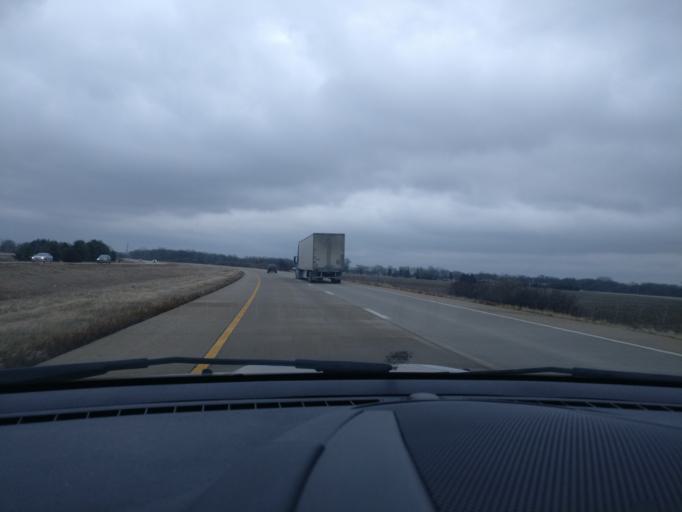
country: US
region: Illinois
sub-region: Whiteside County
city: Prophetstown
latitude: 41.7285
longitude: -89.9113
